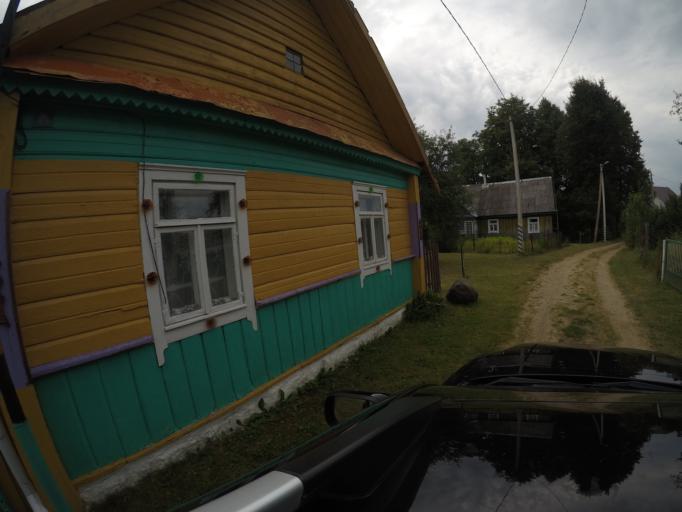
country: BY
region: Grodnenskaya
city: Hal'shany
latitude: 54.2574
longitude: 26.0056
